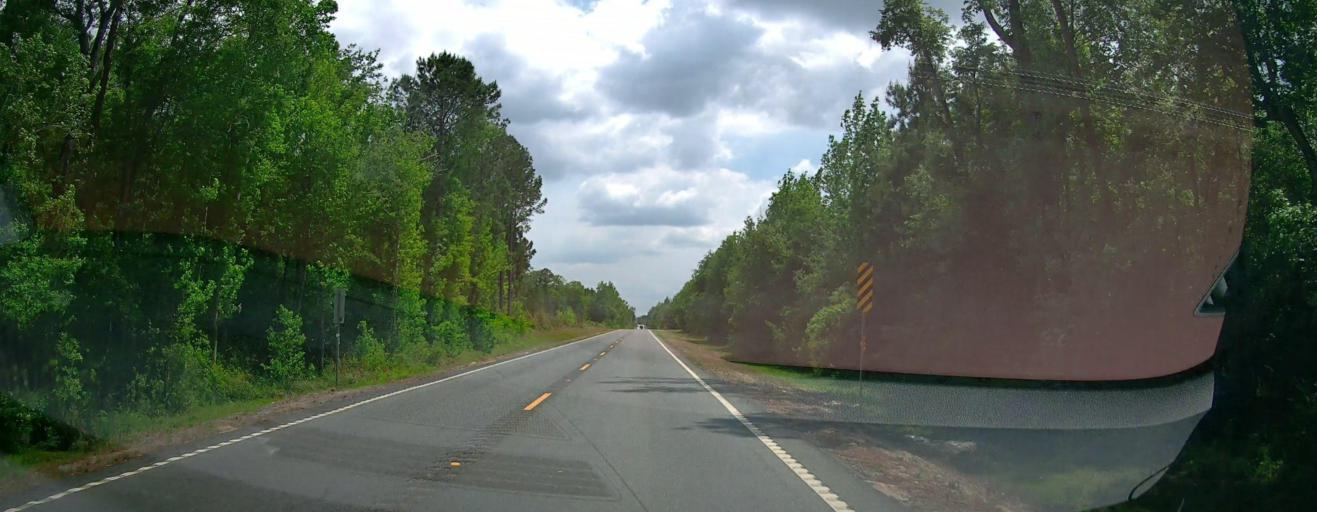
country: US
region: Georgia
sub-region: Treutlen County
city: Soperton
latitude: 32.3961
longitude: -82.6023
